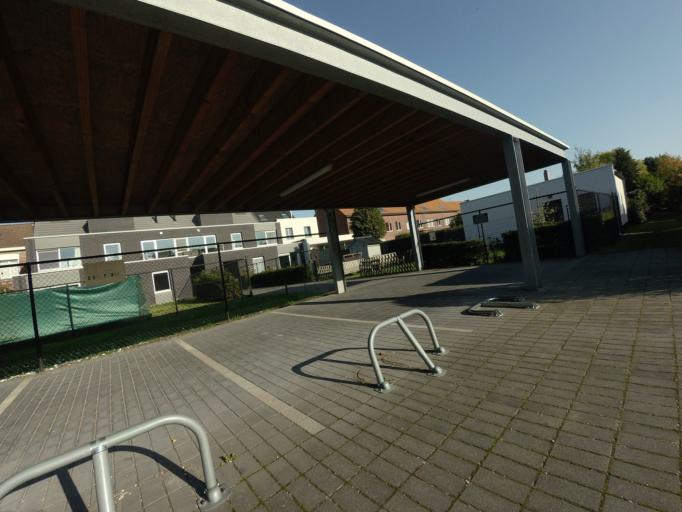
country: BE
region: Flanders
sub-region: Provincie Antwerpen
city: Lint
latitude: 51.1266
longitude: 4.4878
